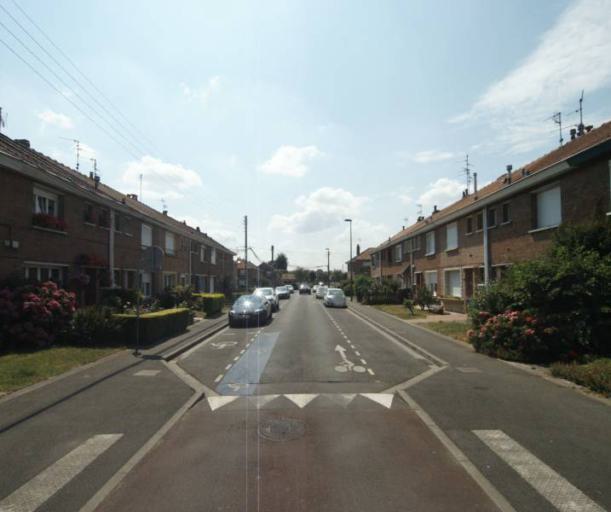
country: FR
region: Nord-Pas-de-Calais
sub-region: Departement du Nord
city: Saint-Andre-lez-Lille
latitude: 50.6588
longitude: 3.0479
